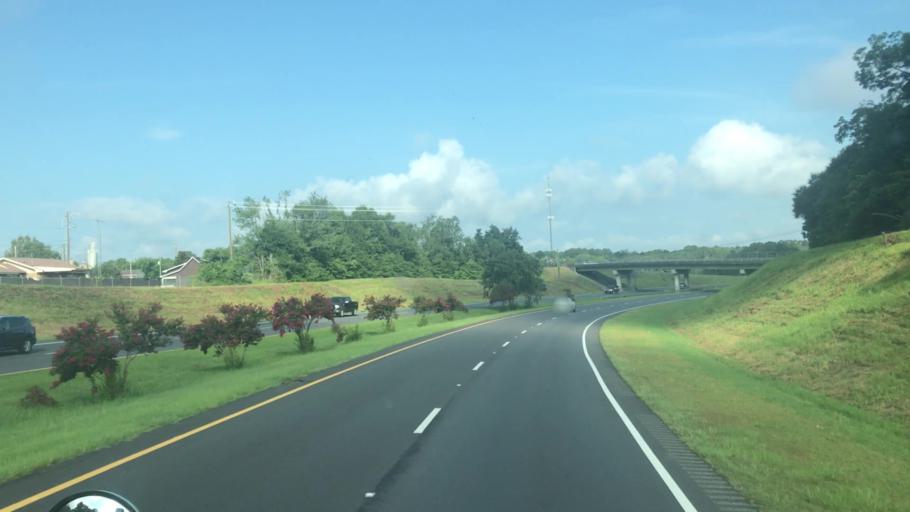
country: US
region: Georgia
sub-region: Decatur County
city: Bainbridge
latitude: 30.8924
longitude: -84.5775
